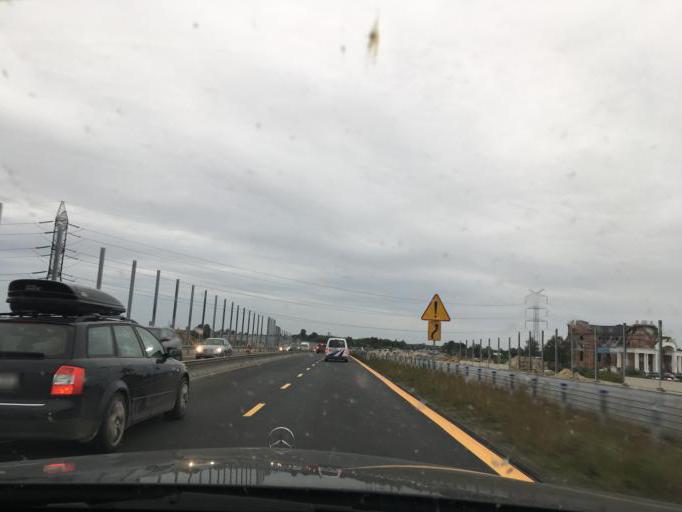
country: PL
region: Masovian Voivodeship
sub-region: Powiat wolominski
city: Radzymin
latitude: 52.4098
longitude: 21.2074
